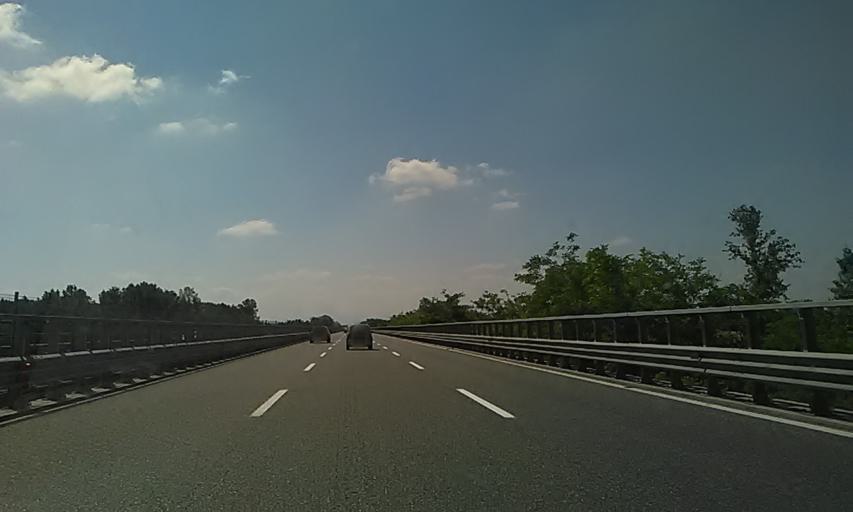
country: IT
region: Piedmont
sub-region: Provincia di Alessandria
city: Castellazzo Bormida
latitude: 44.8649
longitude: 8.5797
